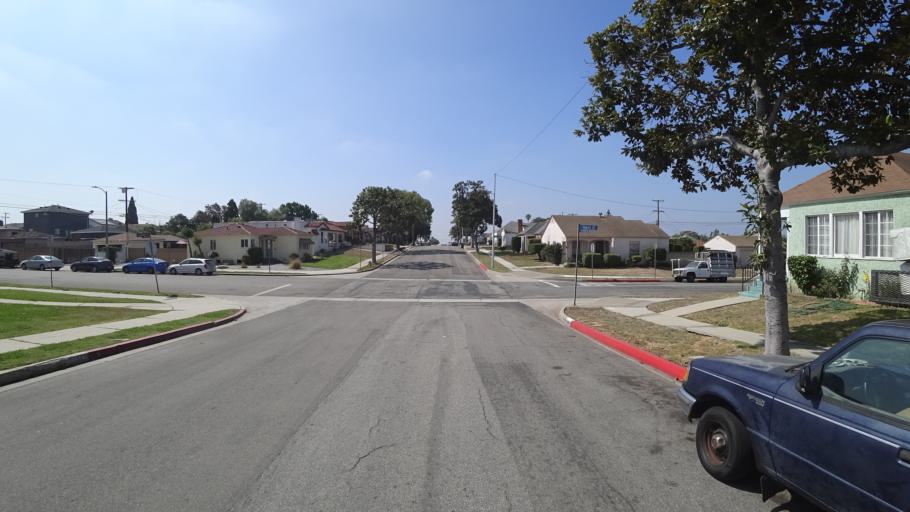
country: US
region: California
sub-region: Los Angeles County
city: Westmont
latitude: 33.9402
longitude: -118.3134
